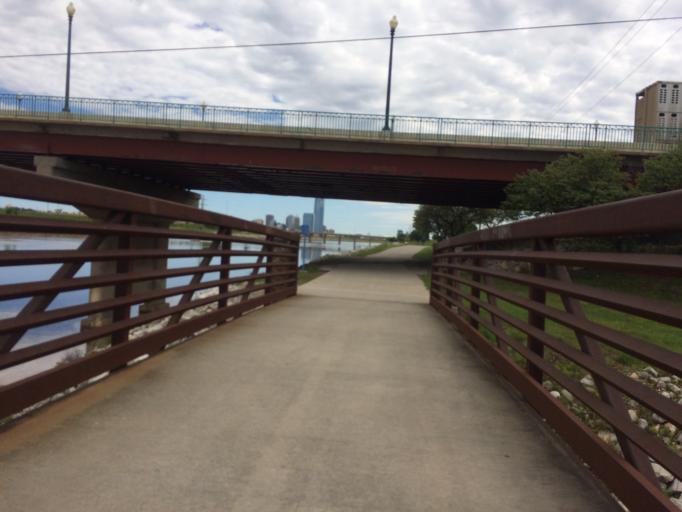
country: US
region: Oklahoma
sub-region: Oklahoma County
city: Oklahoma City
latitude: 35.4585
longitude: -97.5553
